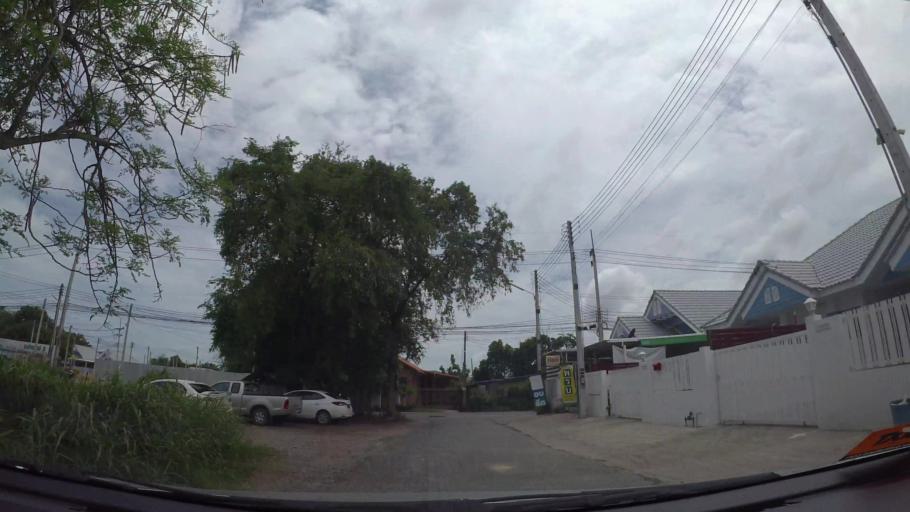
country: TH
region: Chon Buri
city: Sattahip
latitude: 12.6802
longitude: 100.9070
